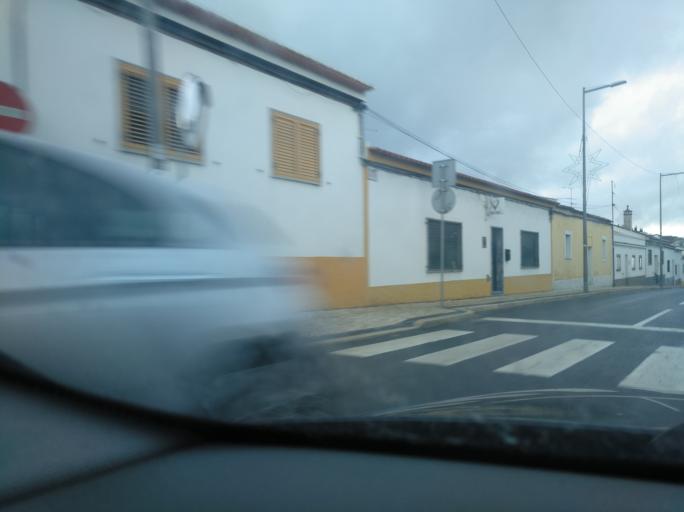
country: PT
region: Beja
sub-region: Aljustrel
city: Aljustrel
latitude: 37.8741
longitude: -8.1677
